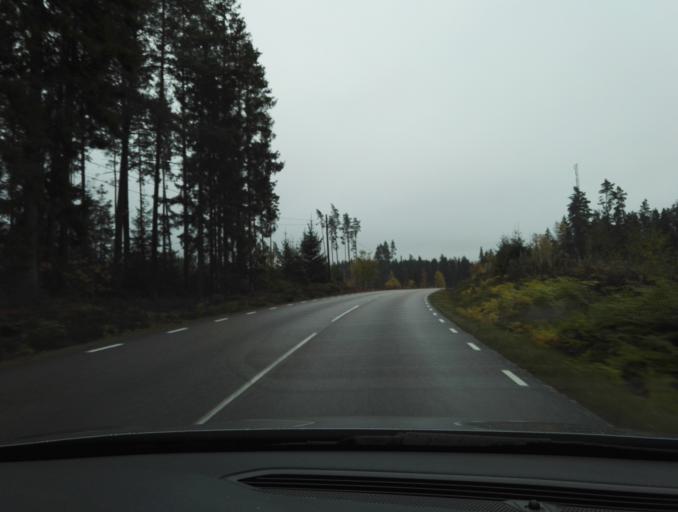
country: SE
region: Kronoberg
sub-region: Vaxjo Kommun
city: Rottne
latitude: 57.0268
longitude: 14.8281
